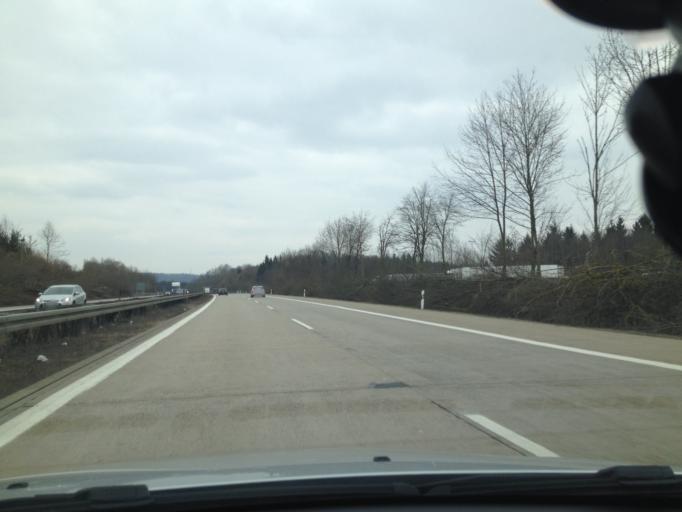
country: DE
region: Baden-Wuerttemberg
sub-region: Regierungsbezirk Stuttgart
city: Ellenberg
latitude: 48.9843
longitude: 10.1947
